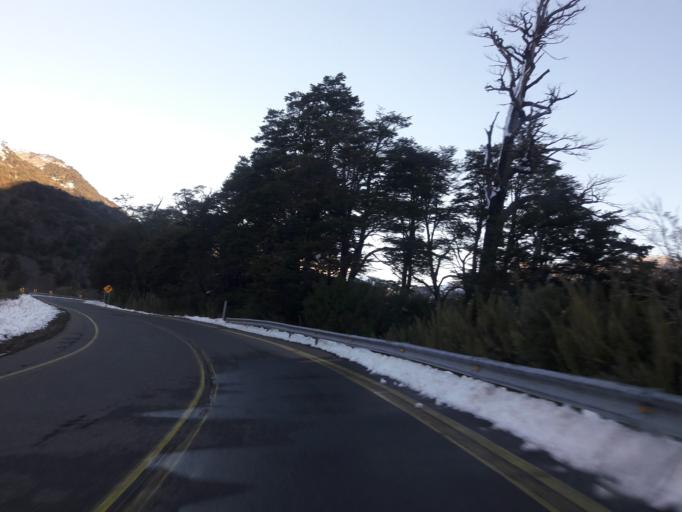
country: CL
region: Araucania
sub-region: Provincia de Cautin
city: Vilcun
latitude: -38.4943
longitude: -71.5220
